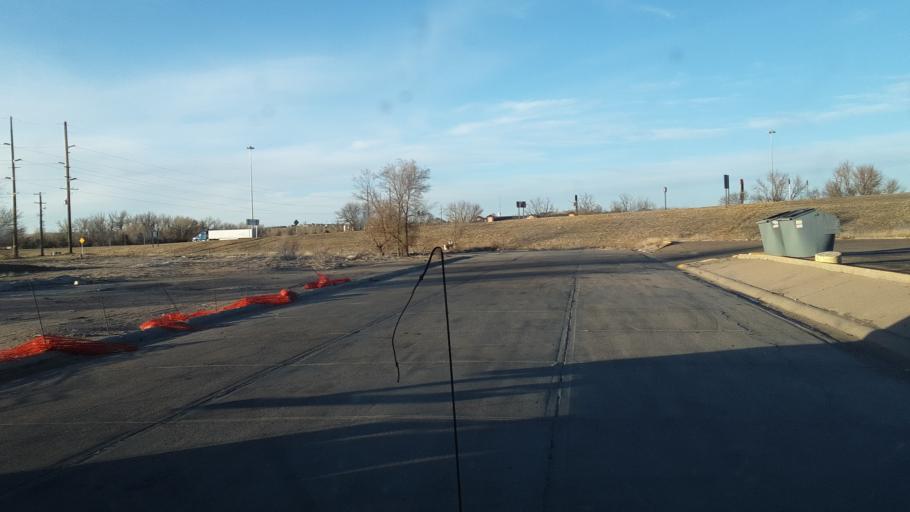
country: US
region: Nebraska
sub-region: Keith County
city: Ogallala
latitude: 41.1131
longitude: -101.7168
